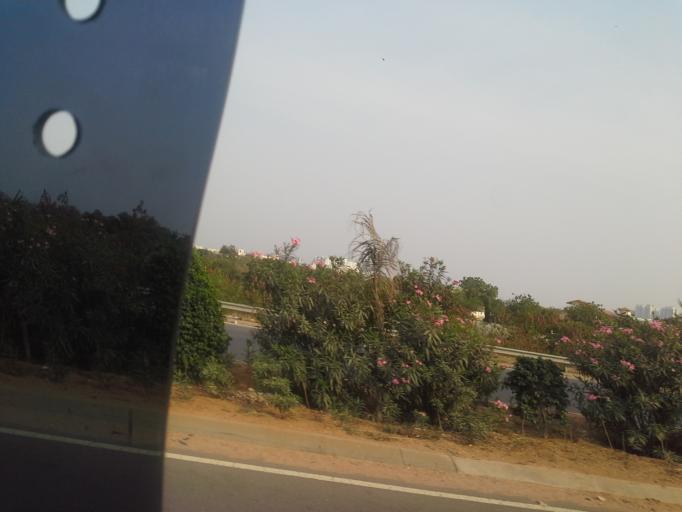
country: IN
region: Telangana
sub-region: Rangareddi
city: Kukatpalli
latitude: 17.4257
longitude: 78.3579
